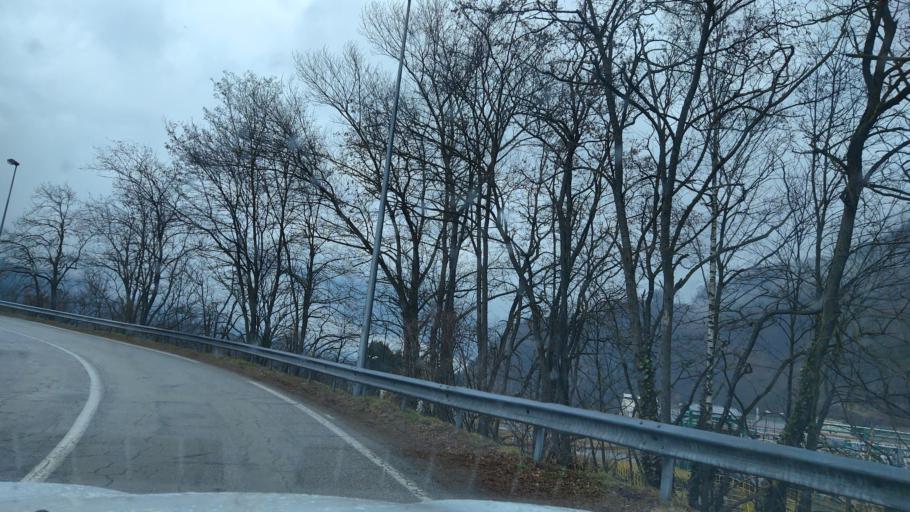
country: FR
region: Rhone-Alpes
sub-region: Departement de la Savoie
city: Saint-Remy-de-Maurienne
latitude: 45.4601
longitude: 6.2941
